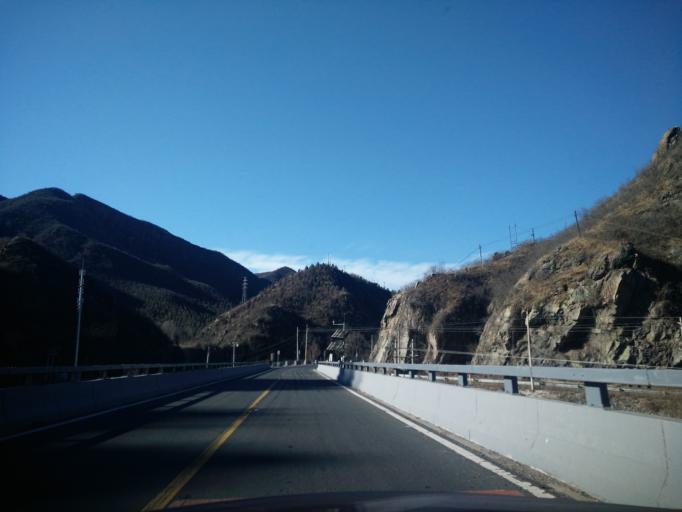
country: CN
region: Beijing
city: Yanchi
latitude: 40.0035
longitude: 115.7865
